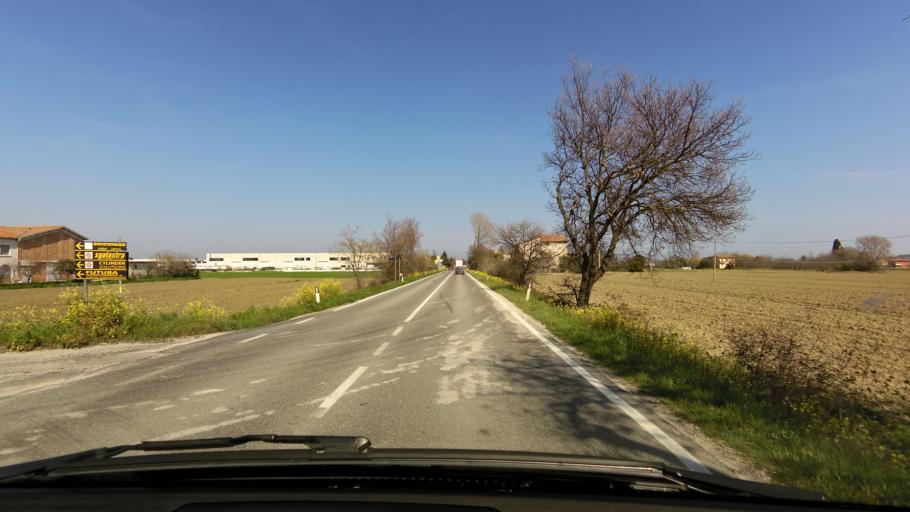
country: IT
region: The Marches
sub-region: Provincia di Macerata
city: Potenza Picena
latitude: 43.3933
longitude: 13.6402
